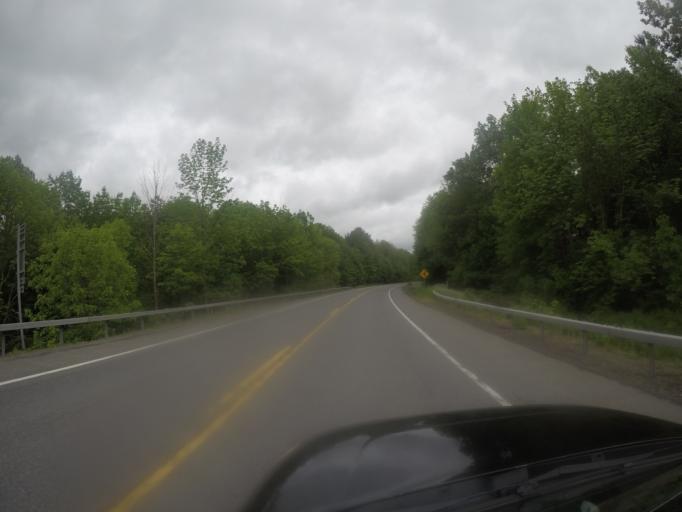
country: US
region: New York
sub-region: Ulster County
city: Shokan
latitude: 42.0857
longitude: -74.3314
